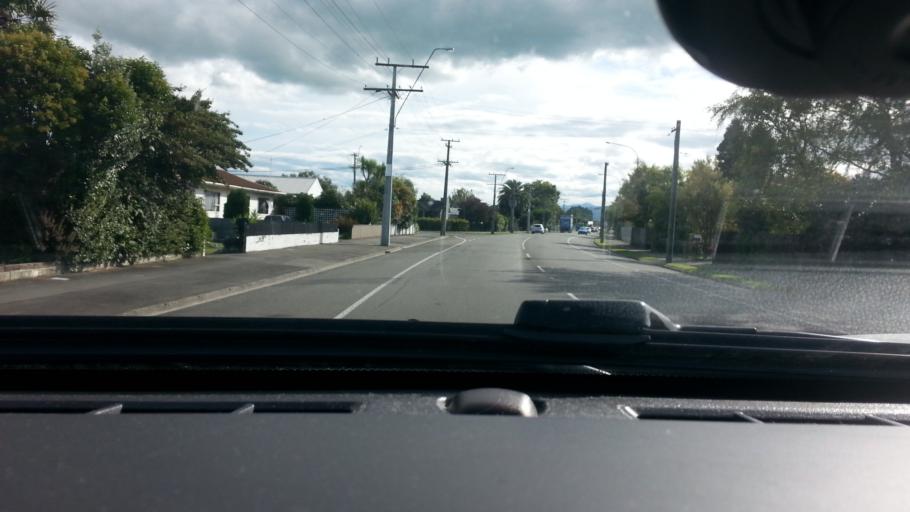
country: NZ
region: Wellington
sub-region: Masterton District
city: Masterton
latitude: -40.9617
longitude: 175.6330
